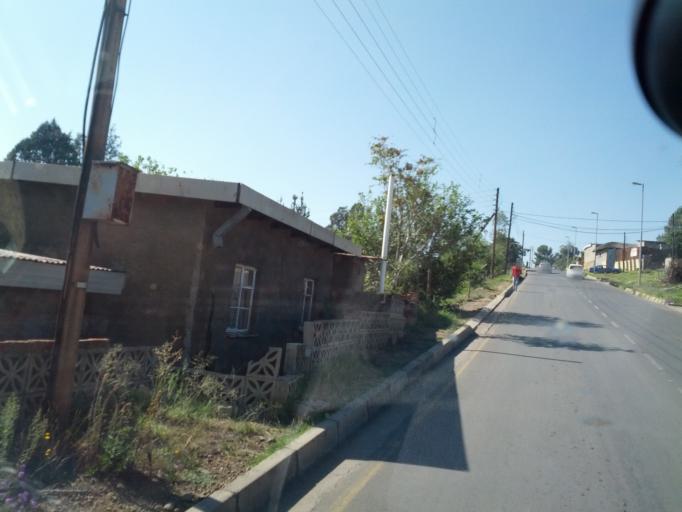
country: LS
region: Maseru
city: Maseru
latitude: -29.3012
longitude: 27.4931
